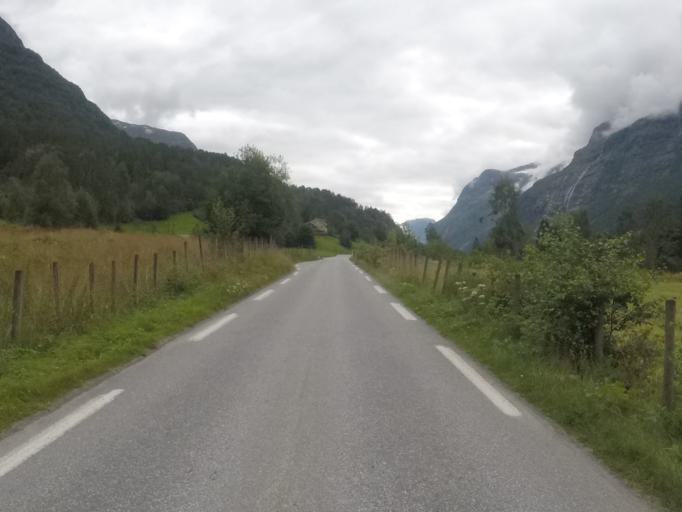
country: NO
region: Sogn og Fjordane
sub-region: Stryn
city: Stryn
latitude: 61.8664
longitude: 6.8824
